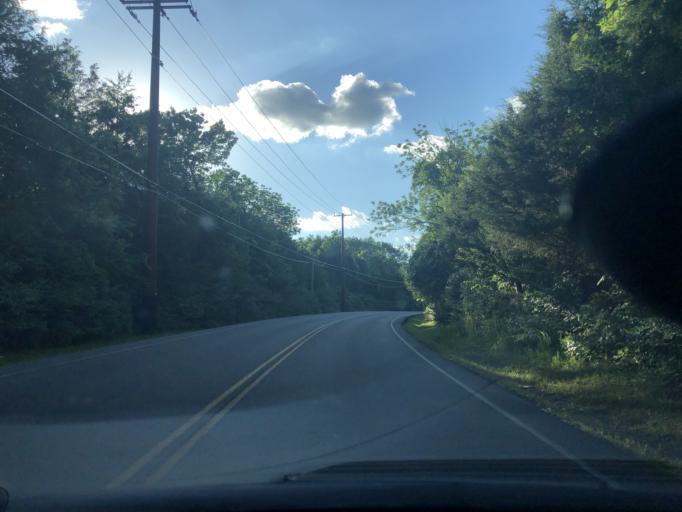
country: US
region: Tennessee
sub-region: Davidson County
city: Forest Hills
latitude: 36.0614
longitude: -86.8378
